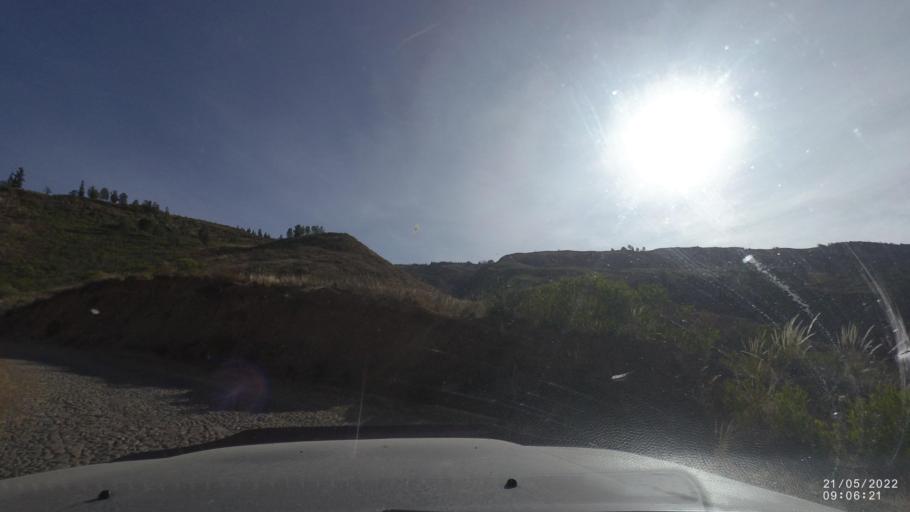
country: BO
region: Cochabamba
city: Cochabamba
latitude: -17.3785
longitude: -66.0221
